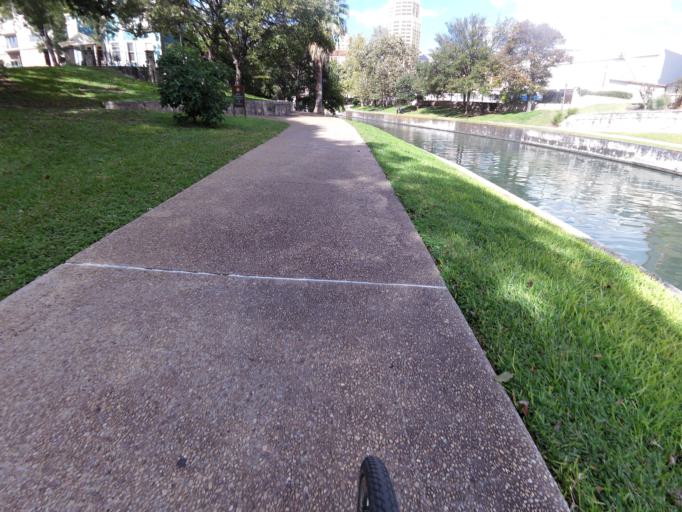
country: US
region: Texas
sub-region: Bexar County
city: San Antonio
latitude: 29.4195
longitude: -98.4924
